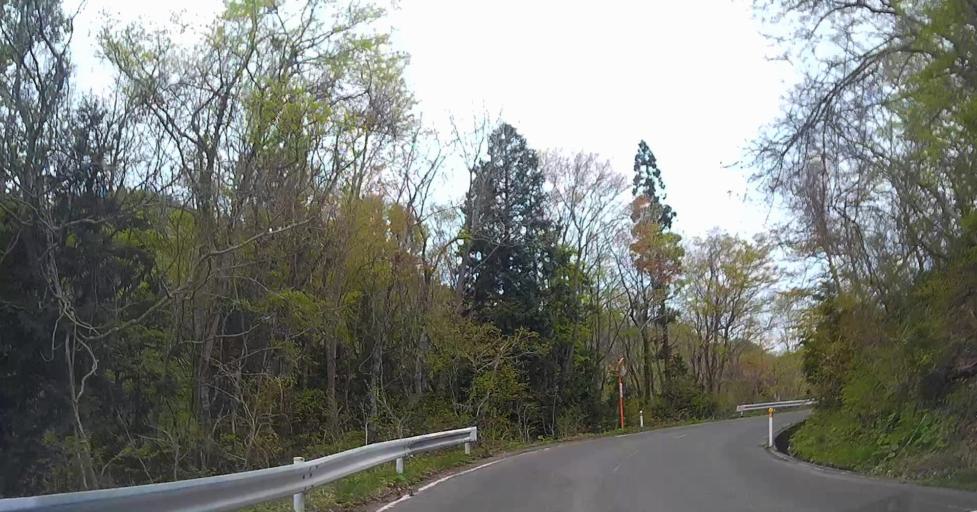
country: JP
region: Aomori
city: Goshogawara
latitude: 40.9047
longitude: 140.5323
